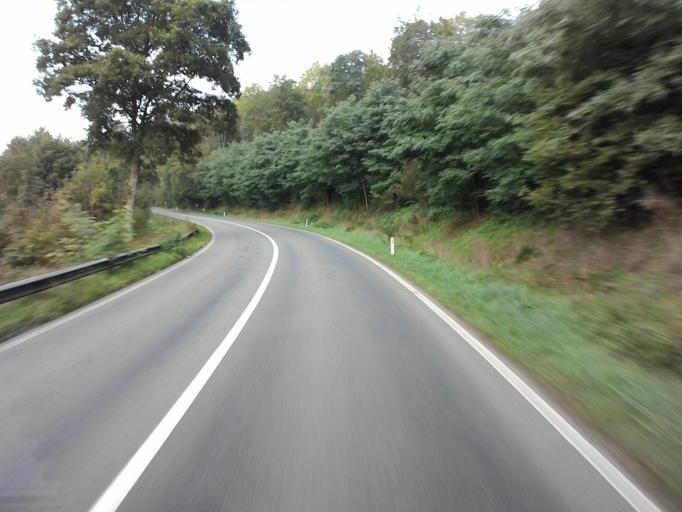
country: BE
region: Wallonia
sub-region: Province du Luxembourg
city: Saint-Leger
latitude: 49.5867
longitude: 5.6063
